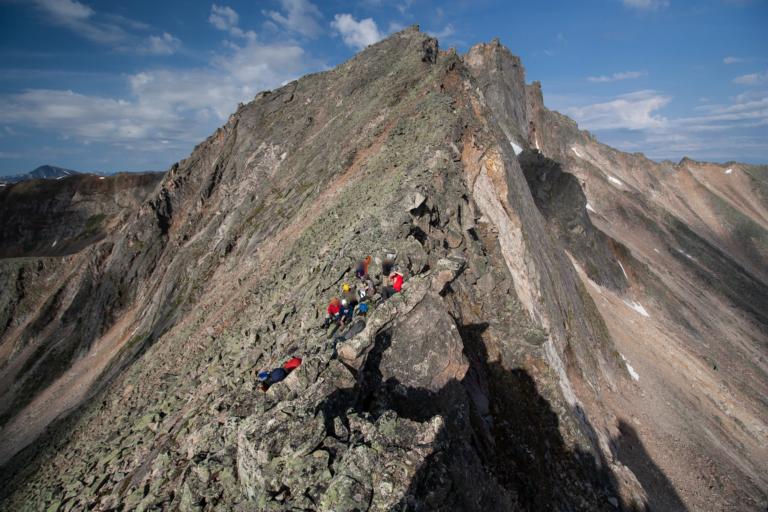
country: RU
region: Respublika Buryatiya
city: Novyy Uoyan
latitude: 56.3113
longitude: 111.2673
